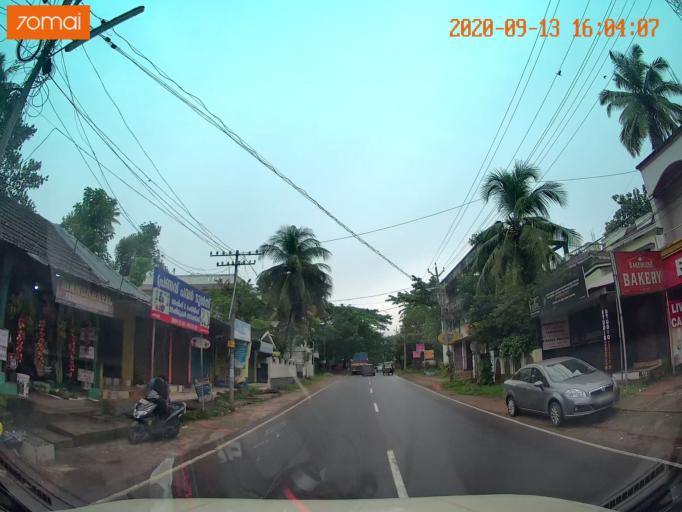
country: IN
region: Kerala
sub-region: Kottayam
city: Palackattumala
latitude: 9.6726
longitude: 76.5680
